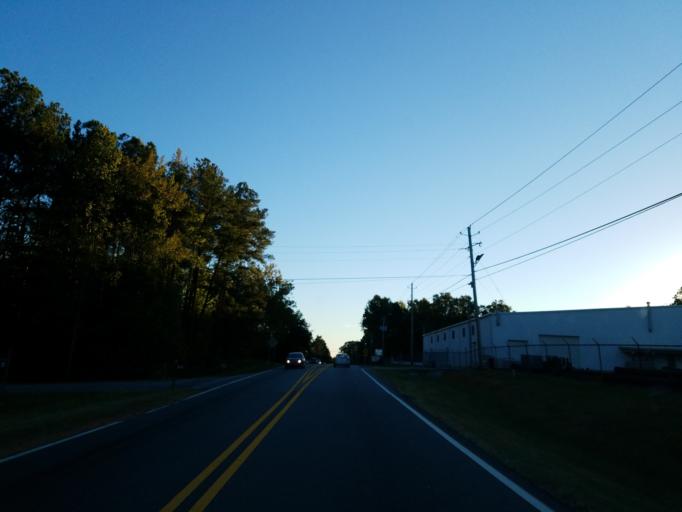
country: US
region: Georgia
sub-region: Forsyth County
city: Cumming
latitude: 34.2475
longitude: -84.1144
